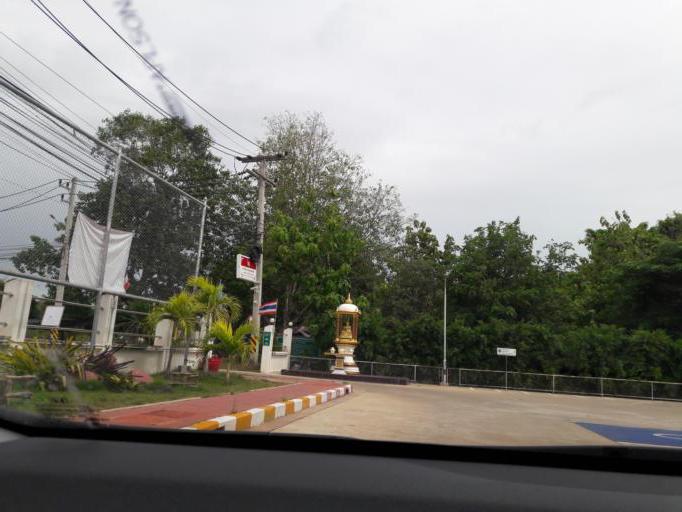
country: TH
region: Samut Sakhon
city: Ban Phaeo
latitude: 13.5524
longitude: 100.0409
